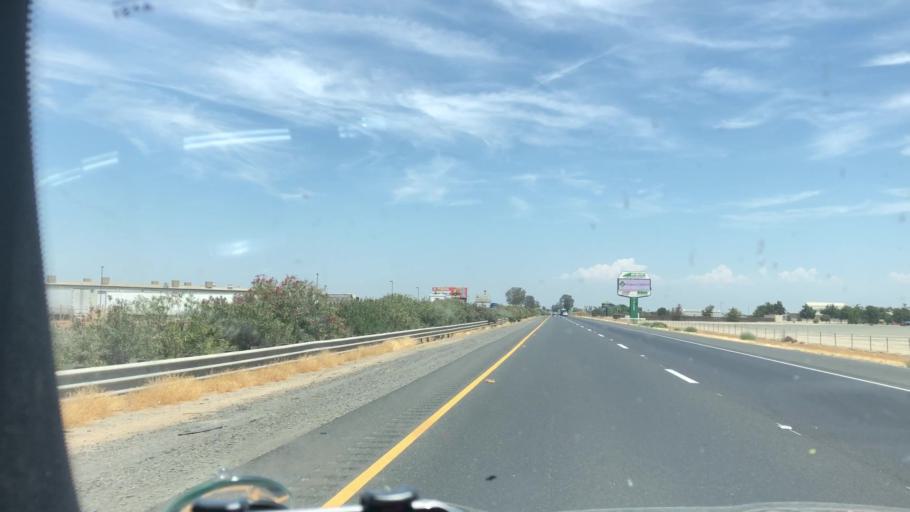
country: US
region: California
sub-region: Tulare County
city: Tulare
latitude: 36.1629
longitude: -119.3320
